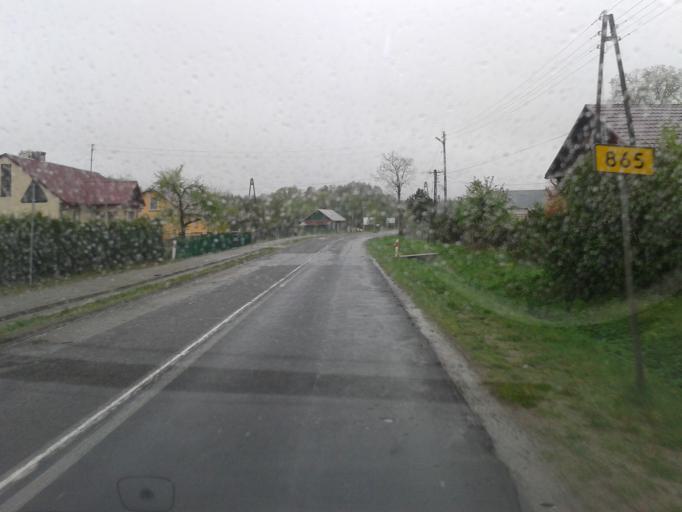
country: PL
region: Subcarpathian Voivodeship
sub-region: Powiat lubaczowski
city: Narol
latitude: 50.3129
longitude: 23.2431
